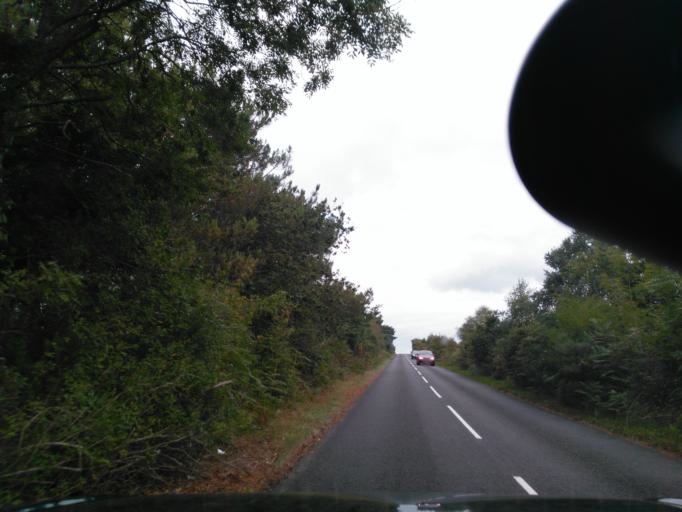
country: GB
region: England
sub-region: Dorset
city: Wareham
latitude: 50.7094
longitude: -2.1081
